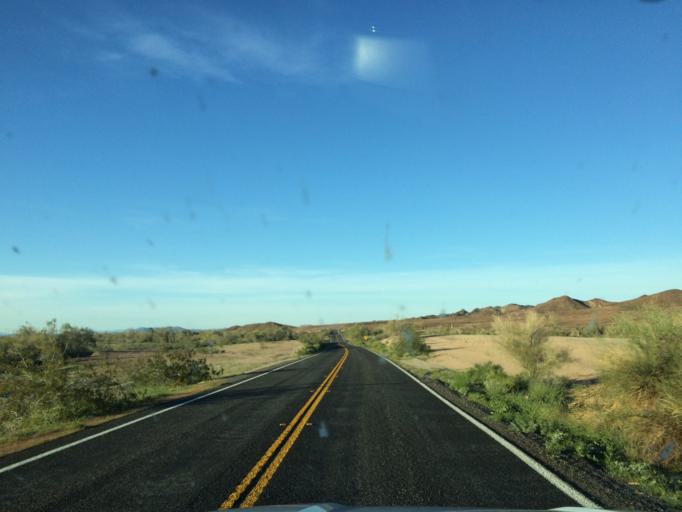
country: MX
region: Baja California
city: Los Algodones
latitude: 33.1487
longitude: -114.8717
